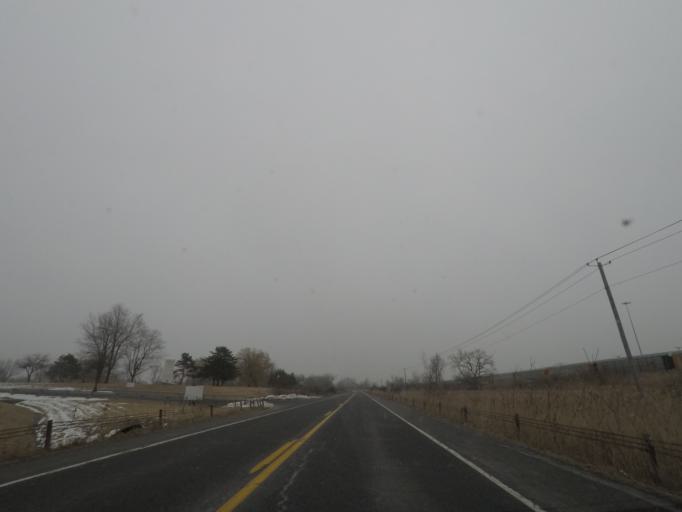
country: US
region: New York
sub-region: Albany County
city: Delmar
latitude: 42.5709
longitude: -73.8561
